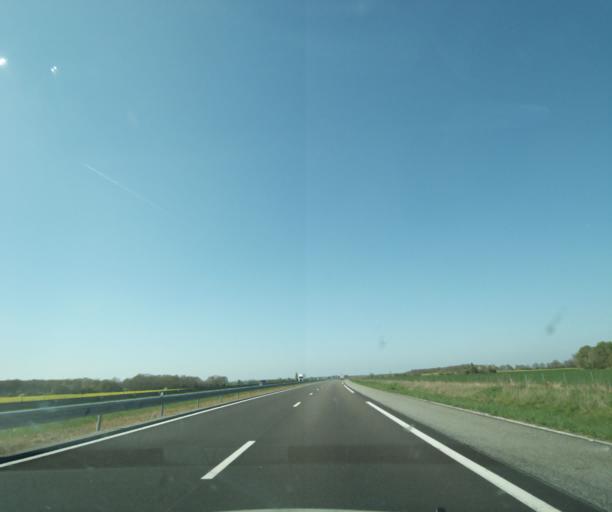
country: FR
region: Centre
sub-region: Departement du Loiret
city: Briare
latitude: 47.6245
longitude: 2.7928
